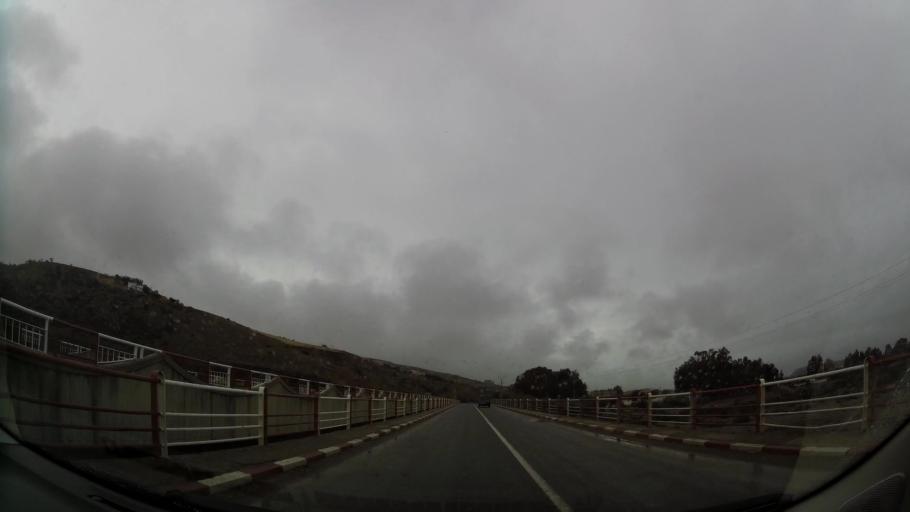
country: MA
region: Taza-Al Hoceima-Taounate
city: Imzourene
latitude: 35.1818
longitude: -3.8804
